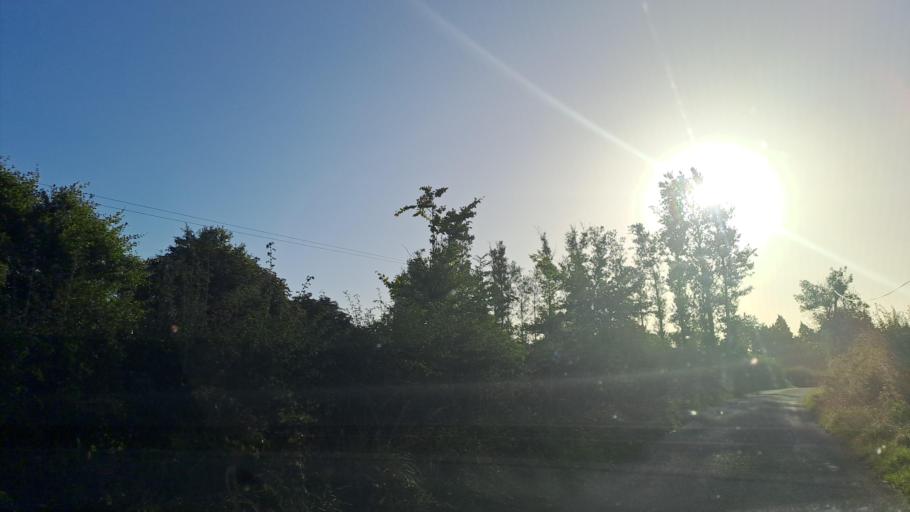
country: IE
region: Ulster
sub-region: An Cabhan
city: Kingscourt
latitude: 53.9812
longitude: -6.8537
